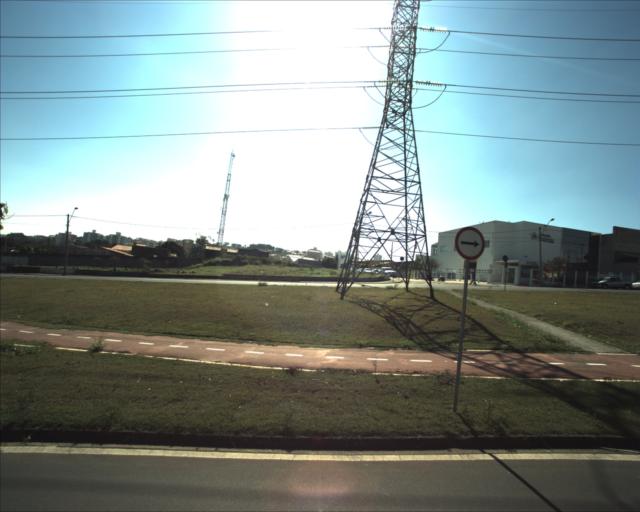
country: BR
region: Sao Paulo
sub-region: Sorocaba
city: Sorocaba
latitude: -23.5131
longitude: -47.4974
